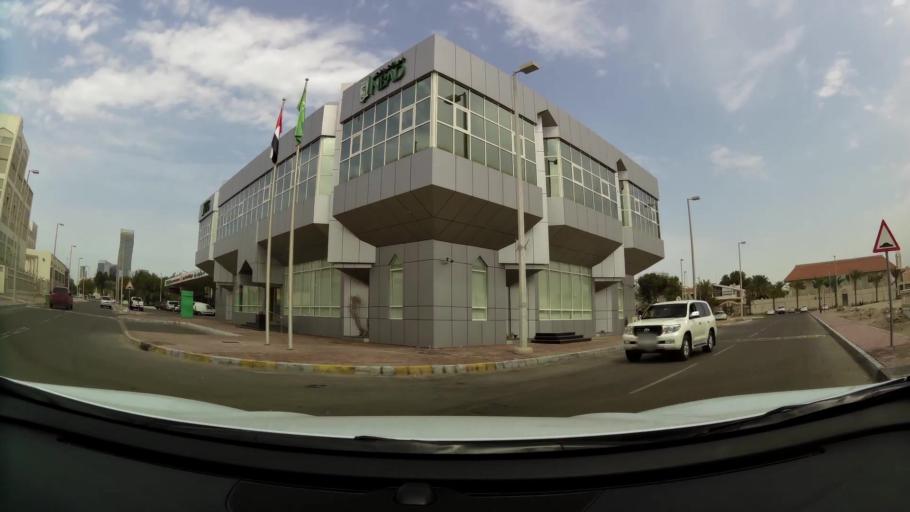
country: AE
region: Abu Dhabi
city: Abu Dhabi
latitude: 24.4595
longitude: 54.3480
